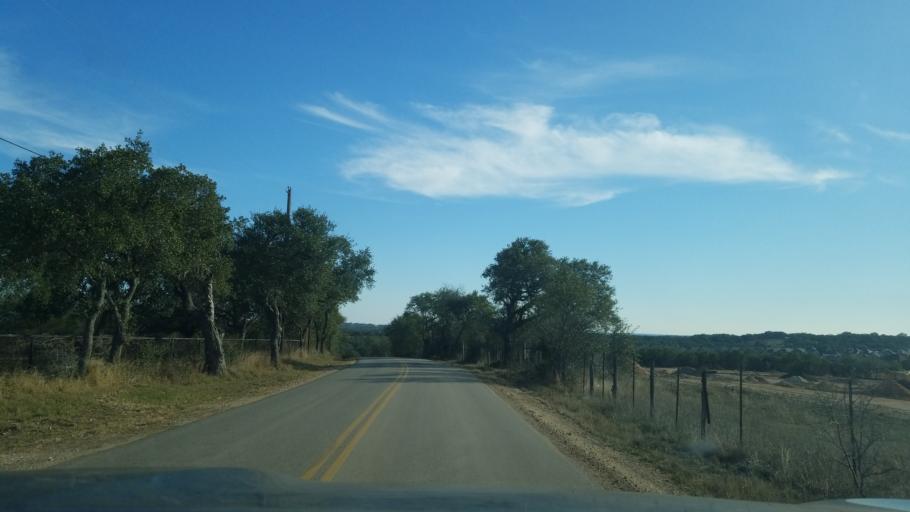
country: US
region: Texas
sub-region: Comal County
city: Canyon Lake
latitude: 29.7855
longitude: -98.2850
